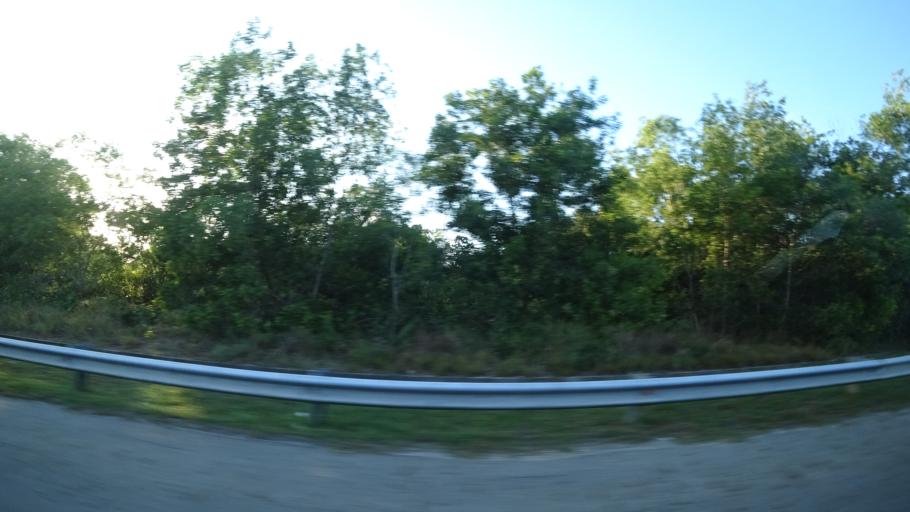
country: BN
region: Tutong
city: Tutong
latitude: 4.7687
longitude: 114.6533
